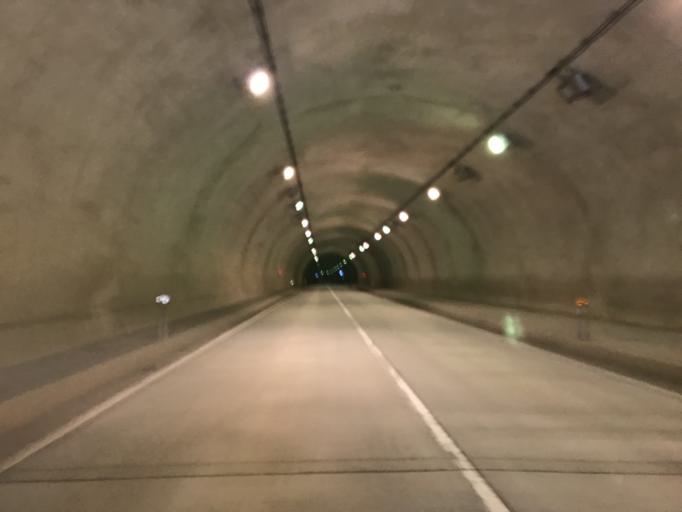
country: JP
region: Fukushima
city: Funehikimachi-funehiki
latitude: 37.6334
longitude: 140.6403
